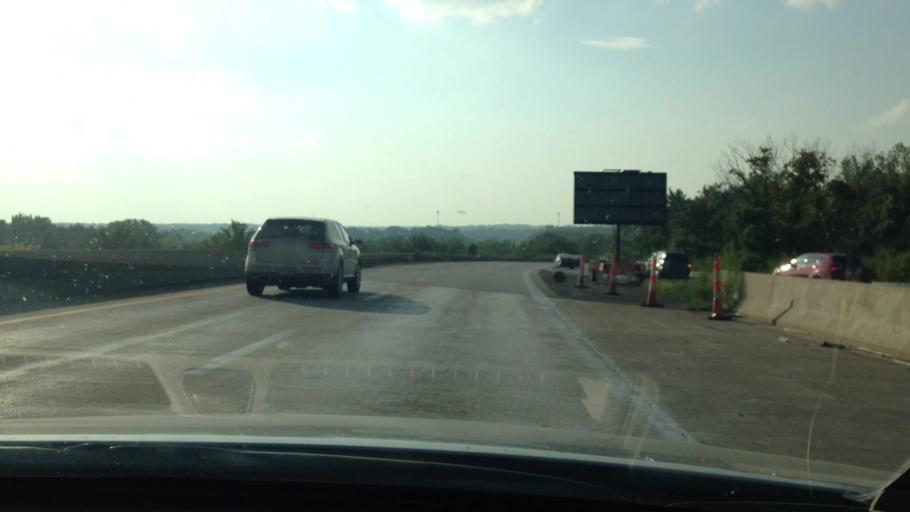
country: US
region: Missouri
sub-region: Platte County
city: Riverside
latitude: 39.1808
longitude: -94.5857
